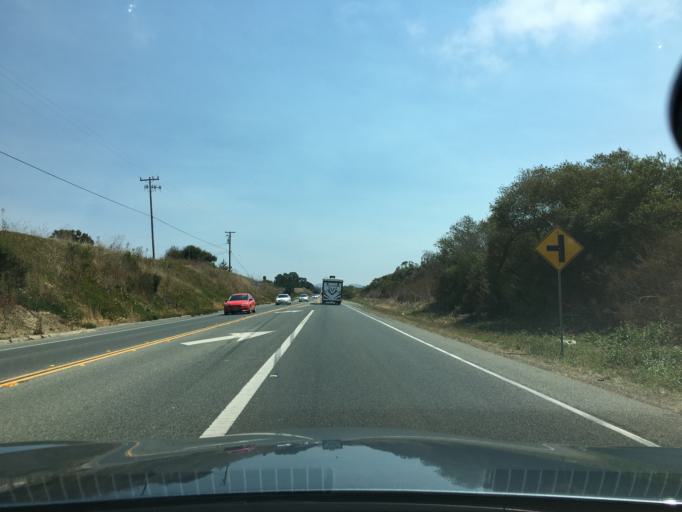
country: US
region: California
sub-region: Monterey County
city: Castroville
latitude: 36.7713
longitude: -121.7336
